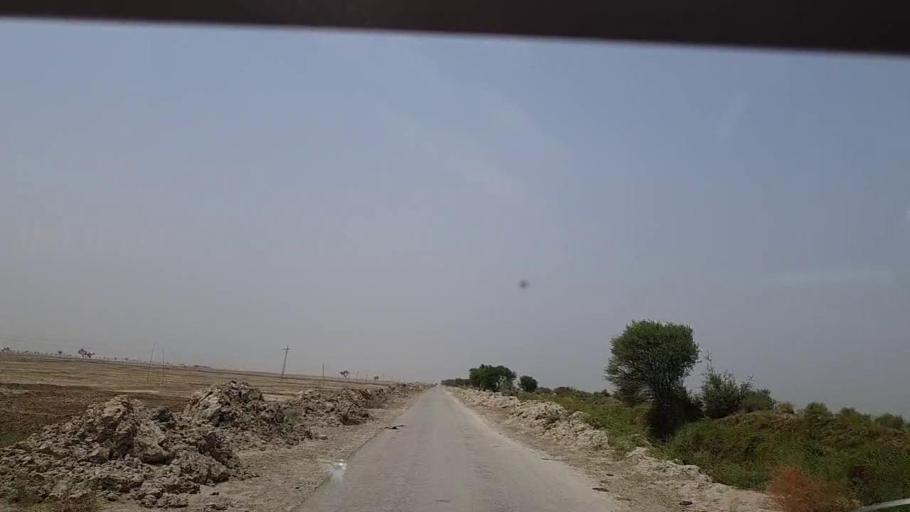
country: PK
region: Sindh
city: Khairpur Nathan Shah
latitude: 27.0200
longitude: 67.6216
